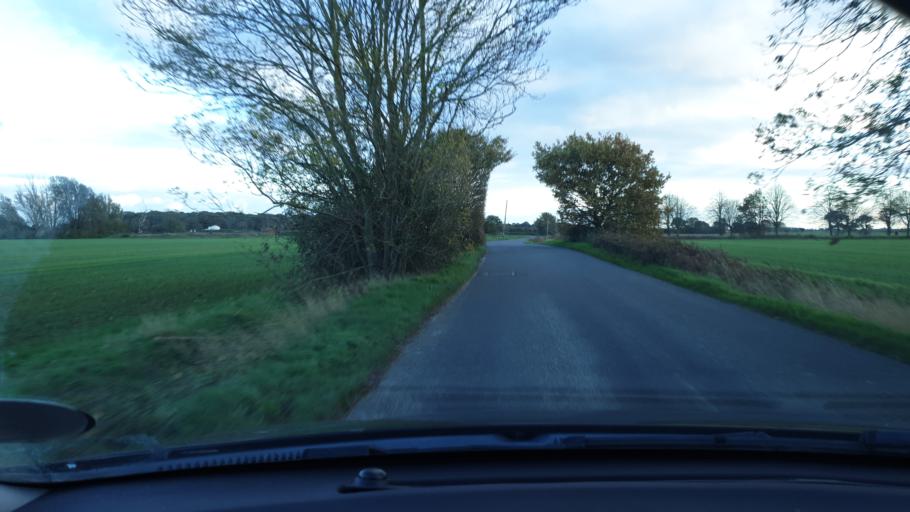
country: GB
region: England
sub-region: Essex
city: Little Clacton
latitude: 51.8923
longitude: 1.1484
